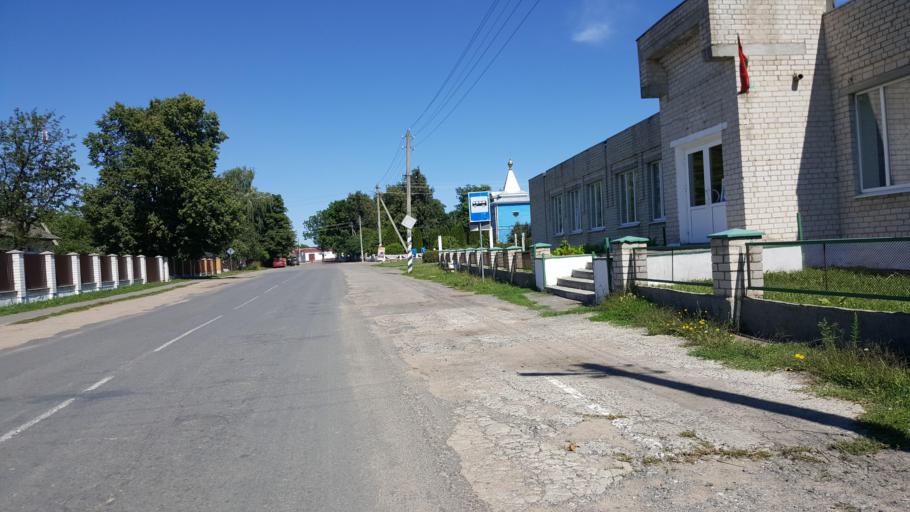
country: BY
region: Brest
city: Charnawchytsy
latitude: 52.2190
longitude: 23.7398
